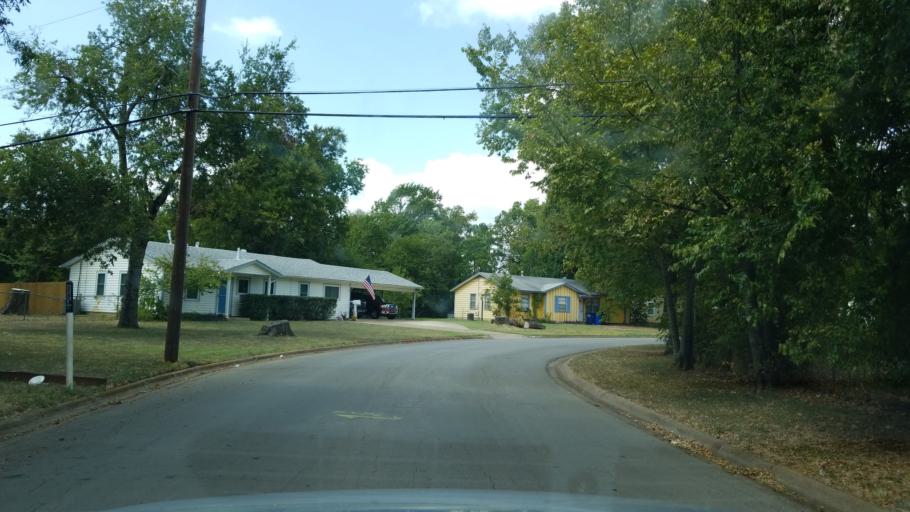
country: US
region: Texas
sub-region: Tarrant County
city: Euless
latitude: 32.8464
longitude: -97.0871
